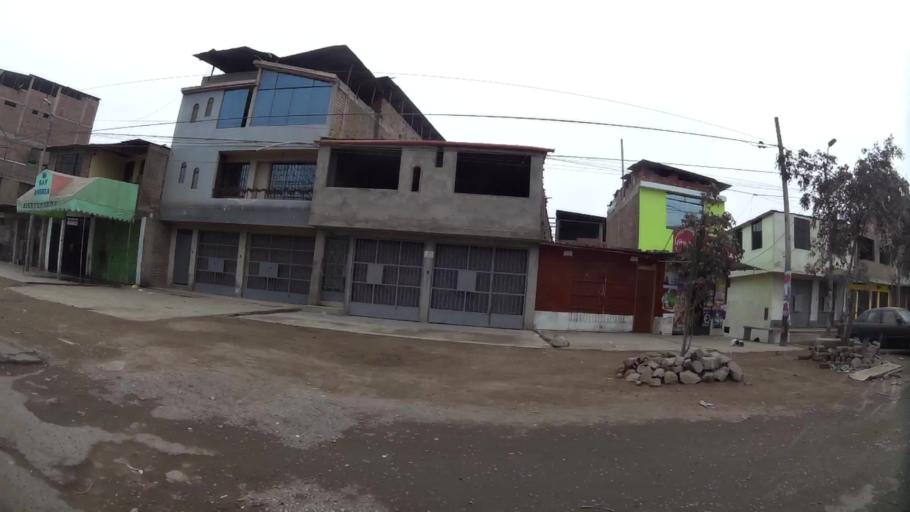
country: PE
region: Lima
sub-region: Lima
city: Surco
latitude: -12.1911
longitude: -76.9340
